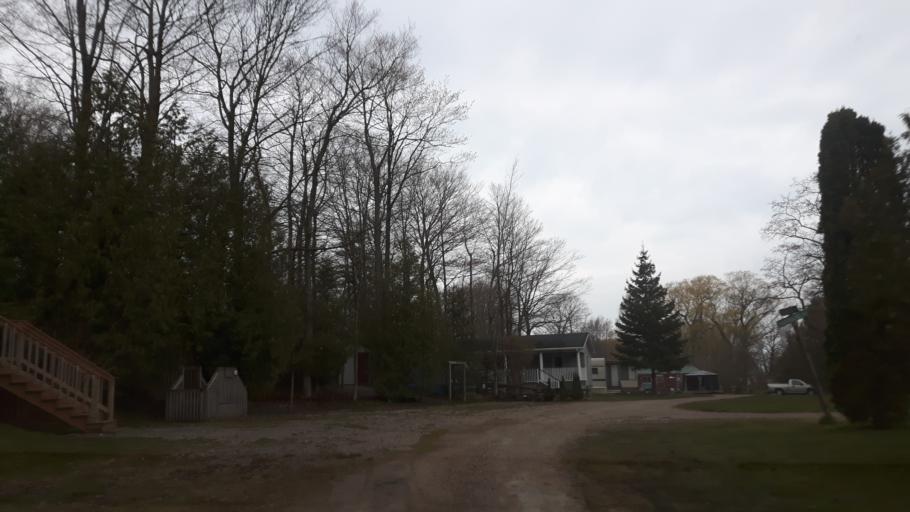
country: CA
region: Ontario
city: Bluewater
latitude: 43.5497
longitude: -81.6963
